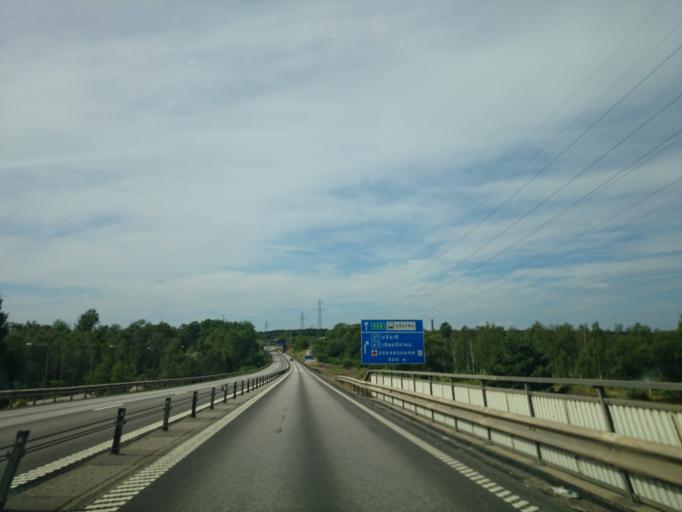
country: SE
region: Kalmar
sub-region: Oskarshamns Kommun
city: Oskarshamn
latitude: 57.2685
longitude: 16.4339
